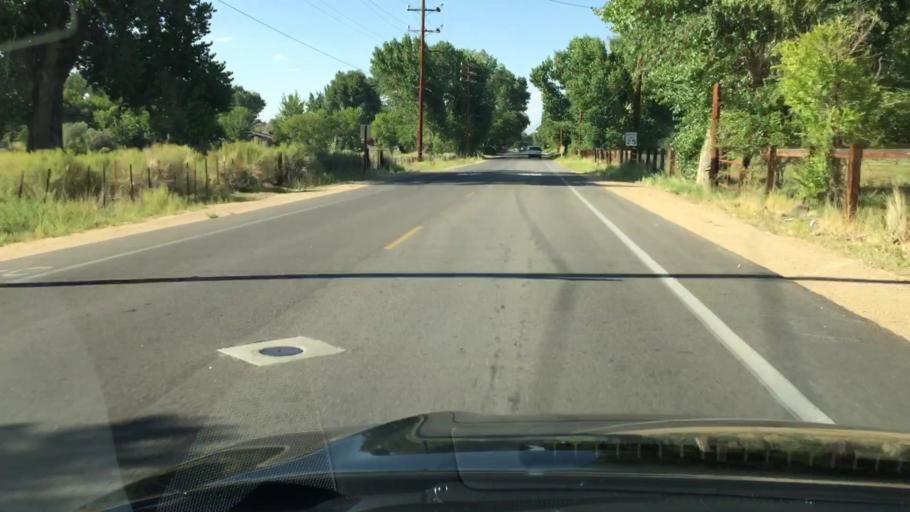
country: US
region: California
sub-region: Inyo County
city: Bishop
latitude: 37.3541
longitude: -118.4046
